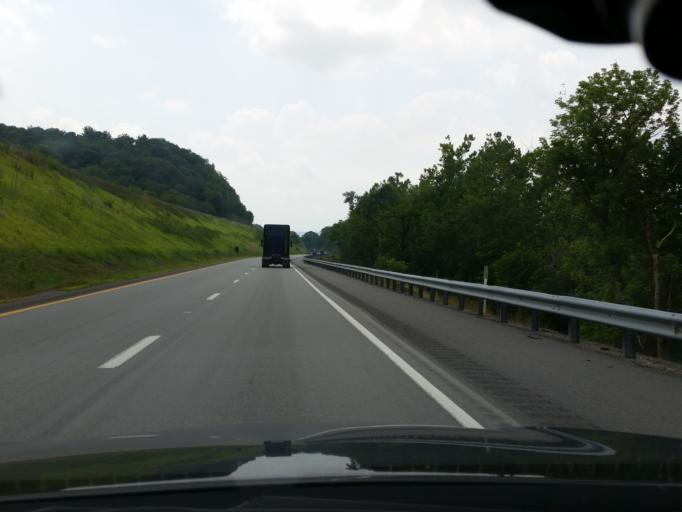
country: US
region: Pennsylvania
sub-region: Perry County
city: Duncannon
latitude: 40.4673
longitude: -77.0307
